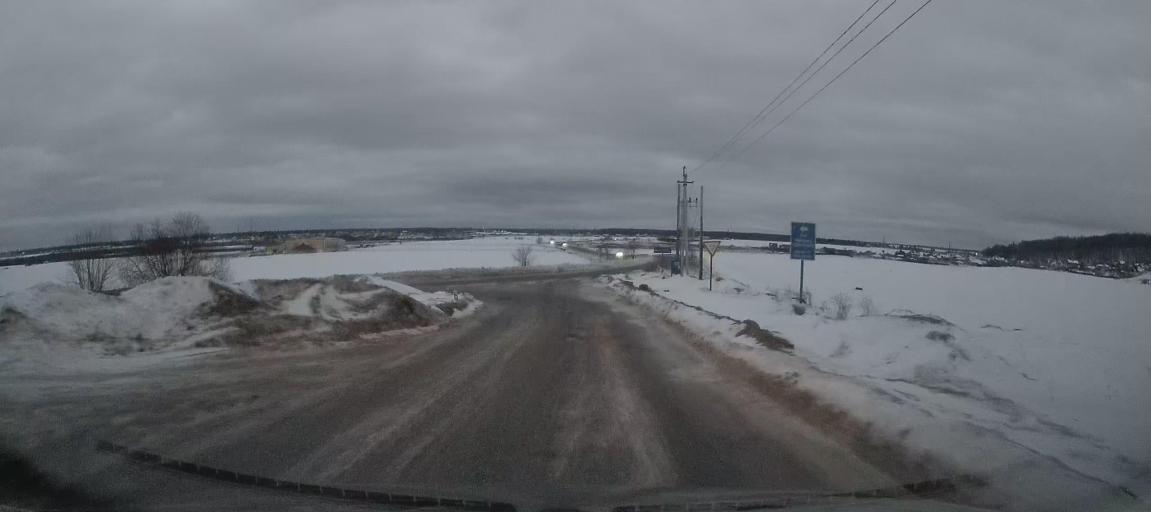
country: RU
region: Leningrad
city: Taytsy
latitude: 59.6925
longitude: 30.1444
